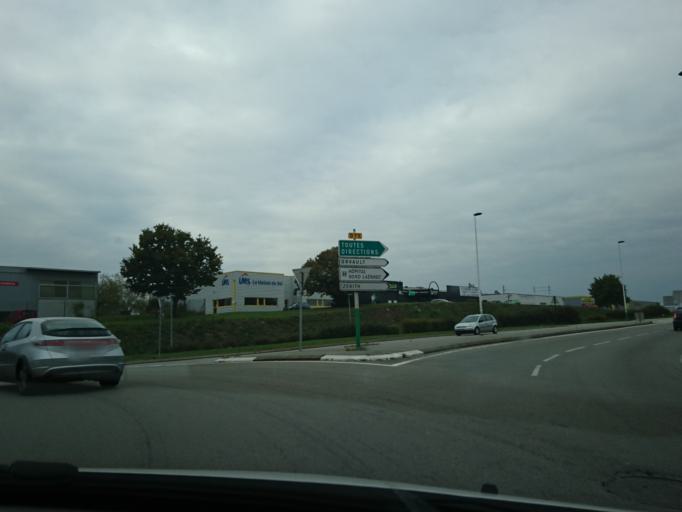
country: FR
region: Pays de la Loire
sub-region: Departement de la Loire-Atlantique
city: Saint-Herblain
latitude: 47.2272
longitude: -1.6513
